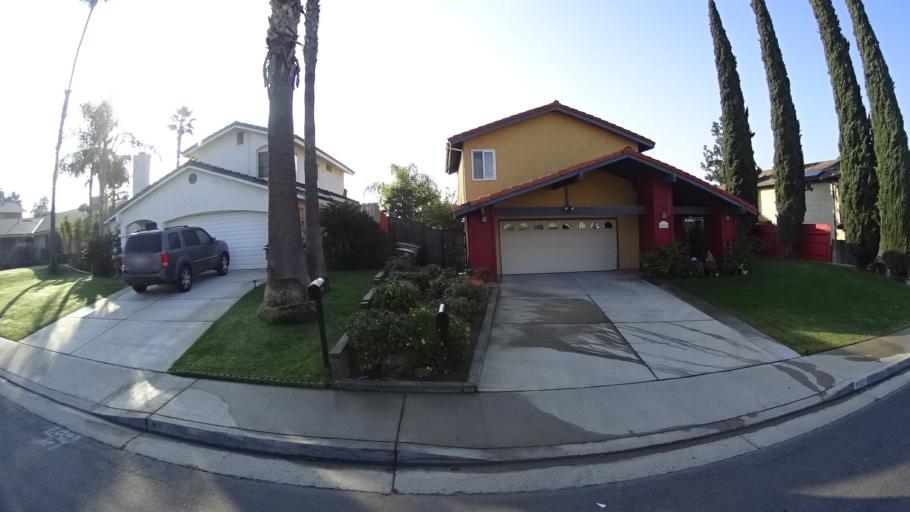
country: US
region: California
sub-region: Kern County
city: Oildale
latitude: 35.4010
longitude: -118.9427
